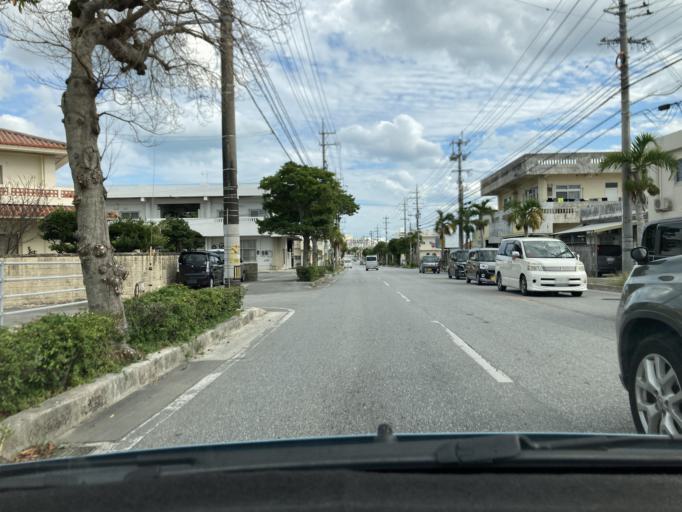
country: JP
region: Okinawa
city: Okinawa
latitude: 26.3580
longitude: 127.8260
